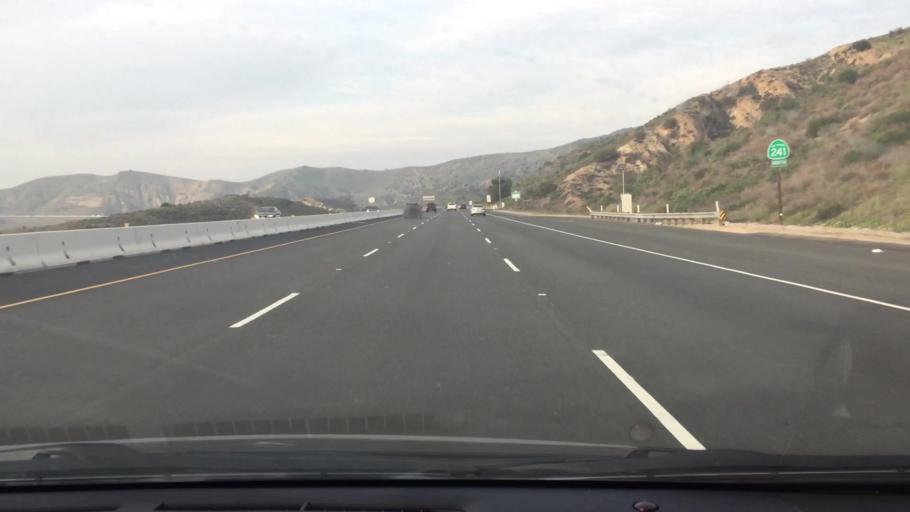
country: US
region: California
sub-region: Orange County
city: Foothill Ranch
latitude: 33.7277
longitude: -117.7185
